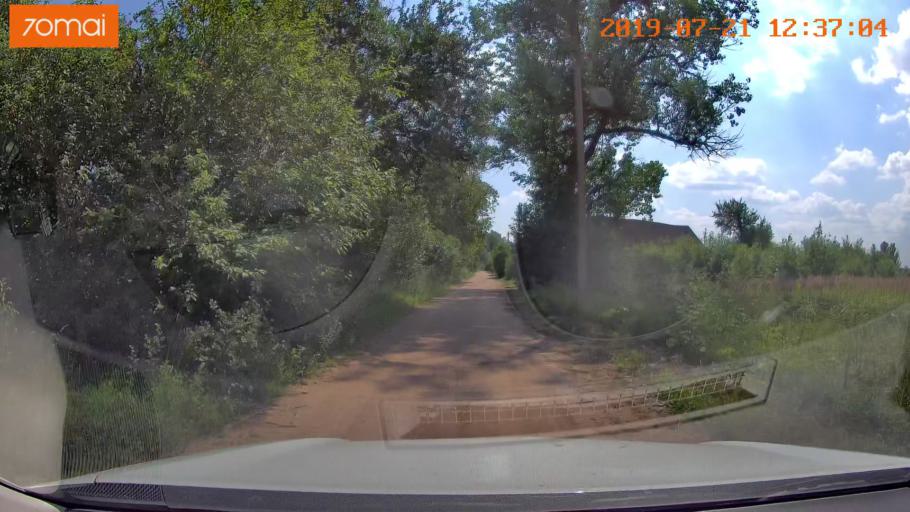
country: BY
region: Grodnenskaya
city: Lyubcha
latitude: 53.8660
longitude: 26.0030
